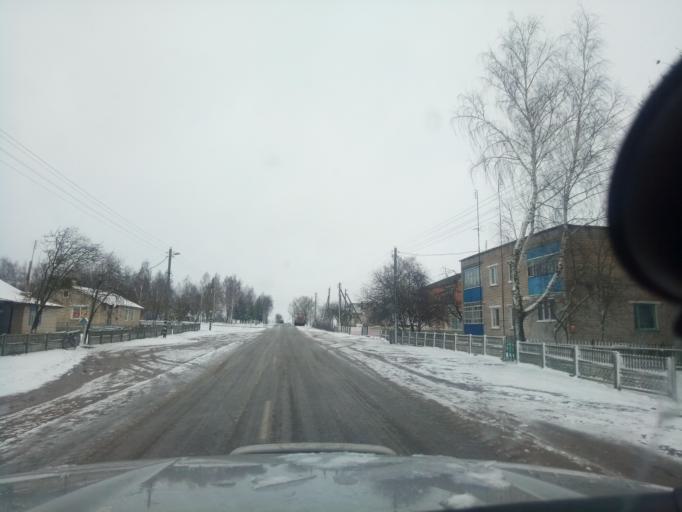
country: BY
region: Minsk
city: Klyetsk
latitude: 53.0512
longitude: 26.7497
